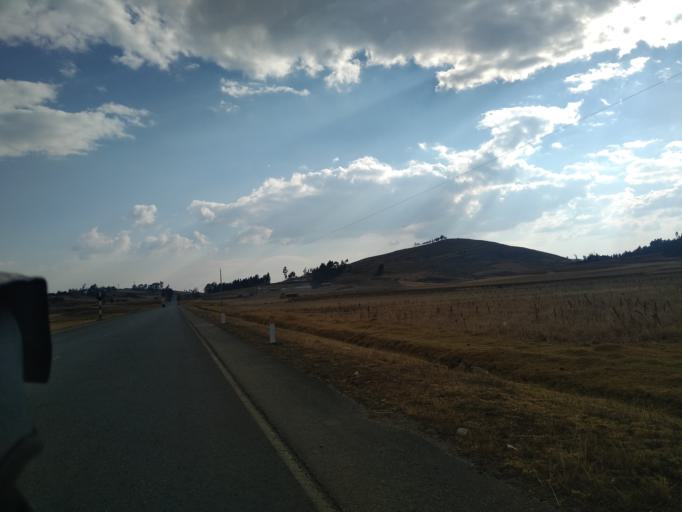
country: PE
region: Cajamarca
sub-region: Provincia de Cajamarca
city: Encanada
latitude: -7.1391
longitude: -78.3875
